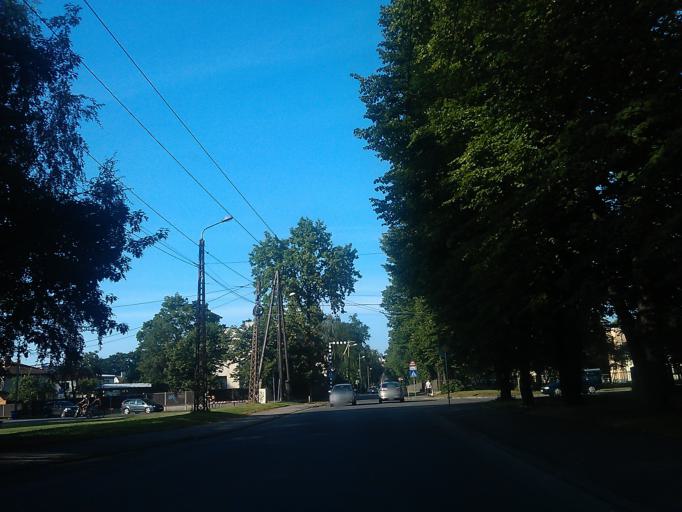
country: LV
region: Riga
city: Jaunciems
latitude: 56.9751
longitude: 24.1825
